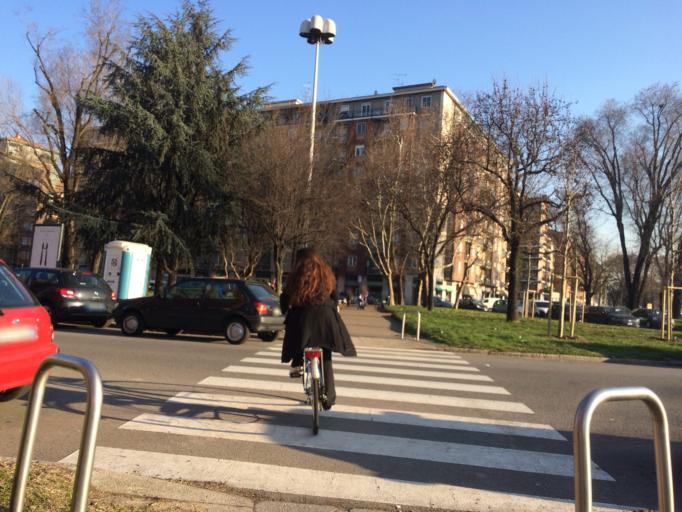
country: IT
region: Lombardy
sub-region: Citta metropolitana di Milano
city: Romano Banco
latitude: 45.4518
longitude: 9.1348
